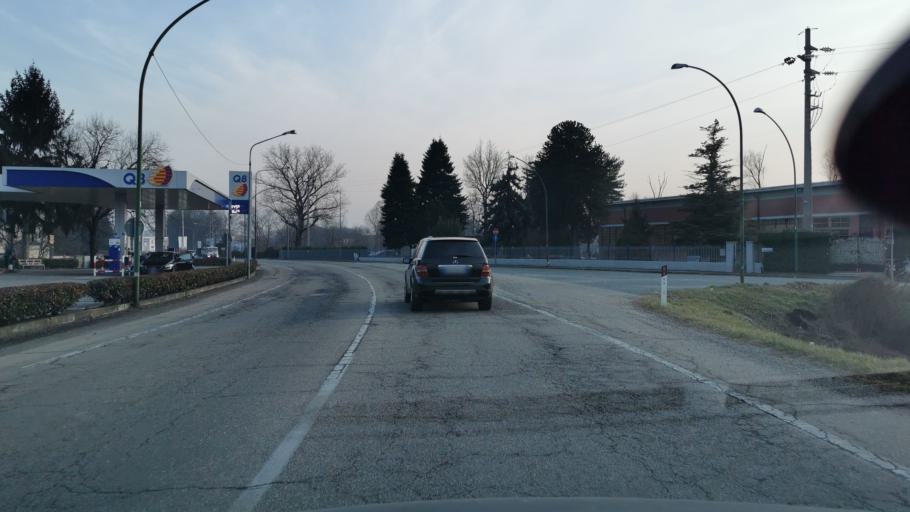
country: IT
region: Piedmont
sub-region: Provincia di Torino
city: Venaria Reale
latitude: 45.1405
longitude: 7.6260
